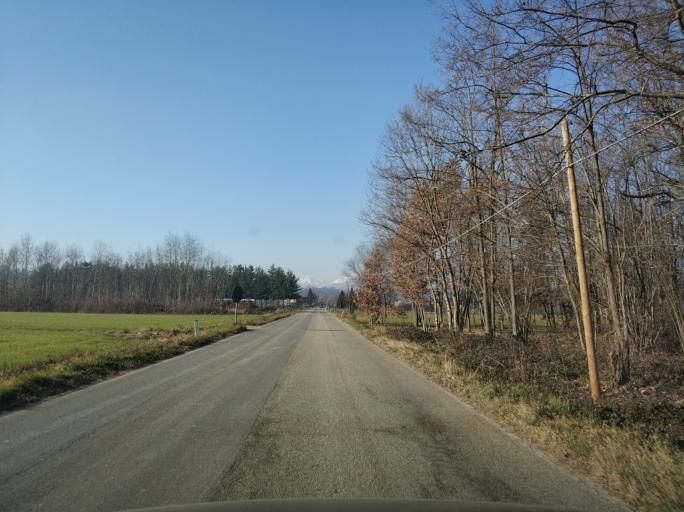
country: IT
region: Piedmont
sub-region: Provincia di Torino
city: Levone
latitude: 45.2988
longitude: 7.6085
